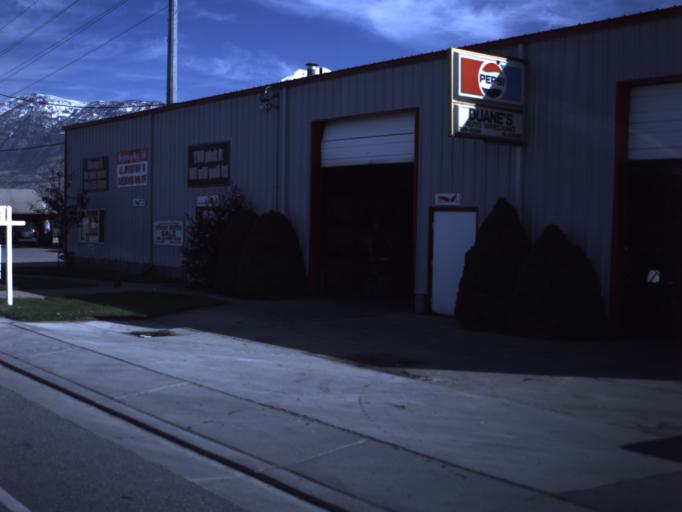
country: US
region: Utah
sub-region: Utah County
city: Lindon
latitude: 40.3184
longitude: -111.7358
